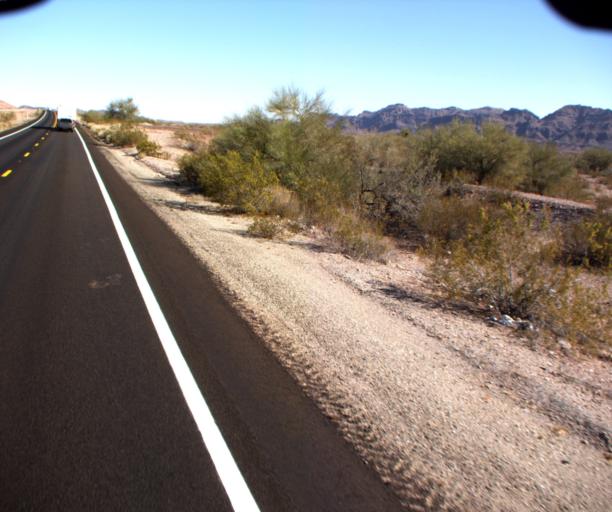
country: US
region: Arizona
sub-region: La Paz County
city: Quartzsite
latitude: 33.1703
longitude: -114.2769
